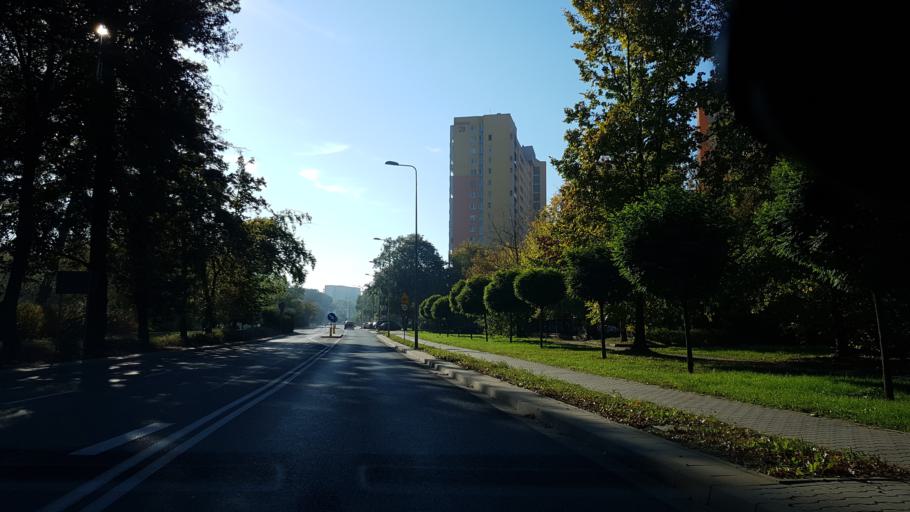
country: PL
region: Masovian Voivodeship
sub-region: Warszawa
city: Zoliborz
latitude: 52.2868
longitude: 20.9772
